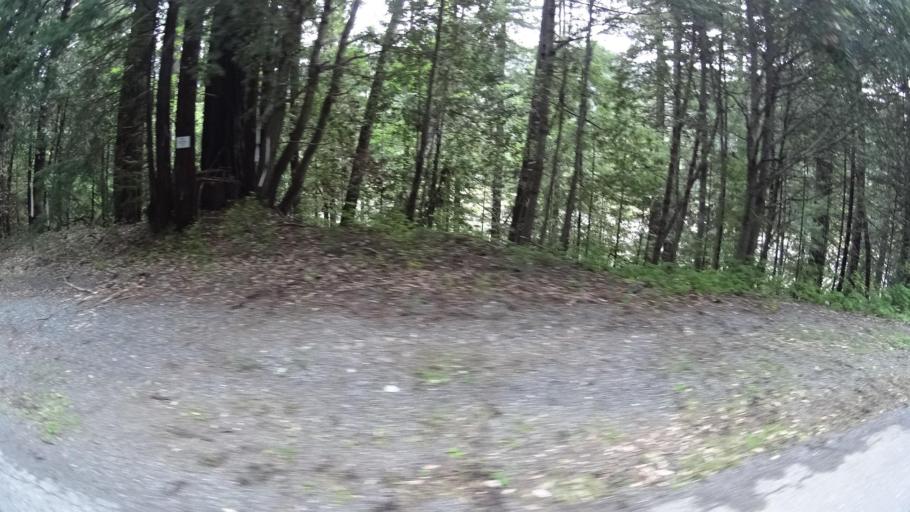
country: US
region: California
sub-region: Humboldt County
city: Redway
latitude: 40.3332
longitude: -123.8462
